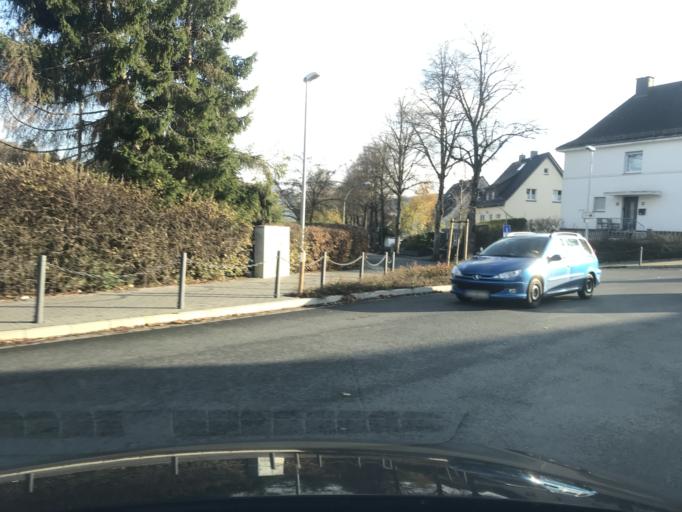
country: DE
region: North Rhine-Westphalia
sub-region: Regierungsbezirk Arnsberg
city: Brilon
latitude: 51.3905
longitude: 8.5716
